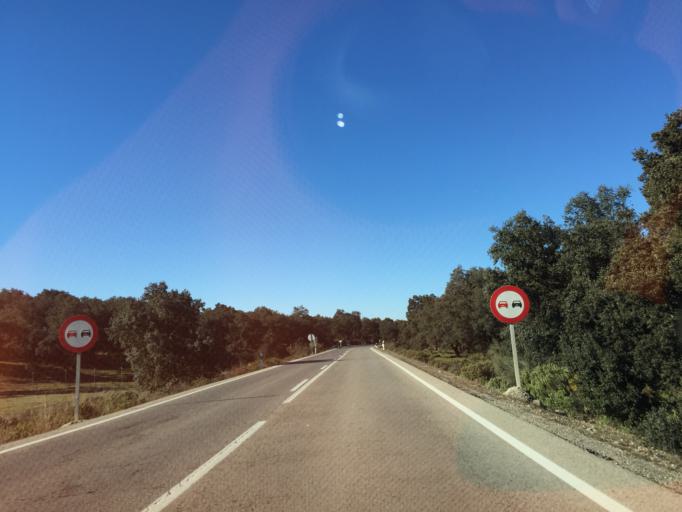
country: ES
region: Andalusia
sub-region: Provincia de Malaga
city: Arriate
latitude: 36.8273
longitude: -5.0896
